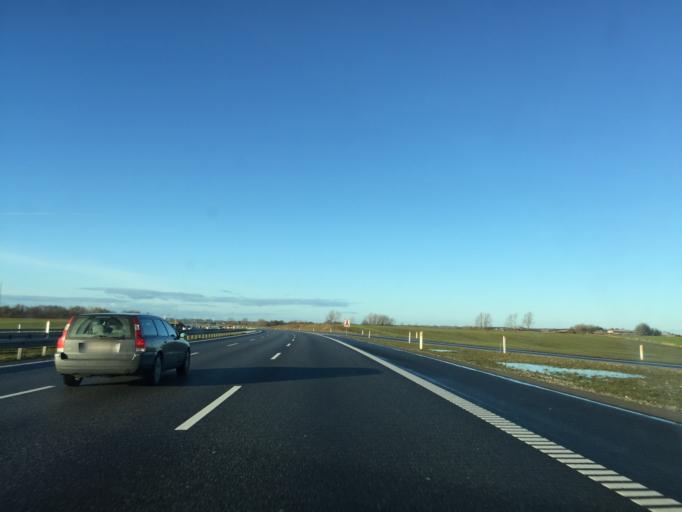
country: DK
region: South Denmark
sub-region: Middelfart Kommune
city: Norre Aby
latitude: 55.4751
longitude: 9.8891
